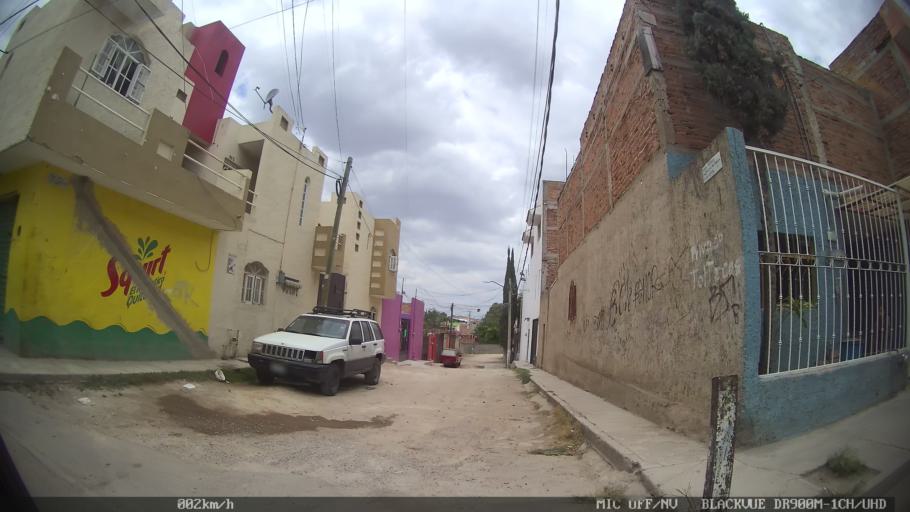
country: MX
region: Jalisco
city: Tonala
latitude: 20.6384
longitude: -103.2608
